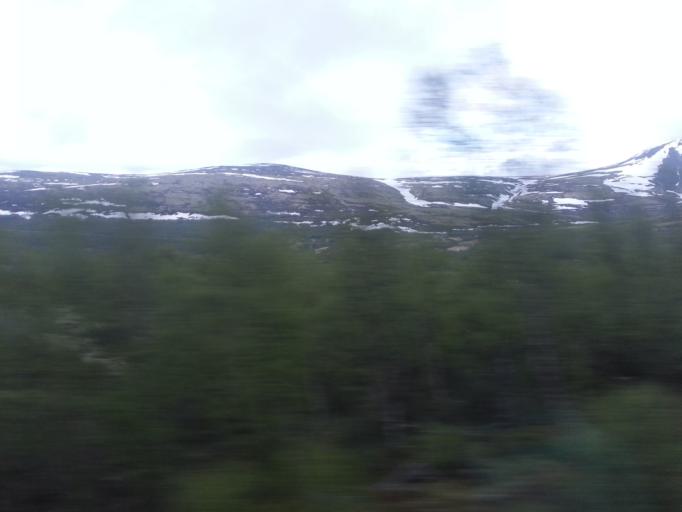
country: NO
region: Oppland
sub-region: Dovre
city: Dovre
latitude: 62.1767
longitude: 9.4506
